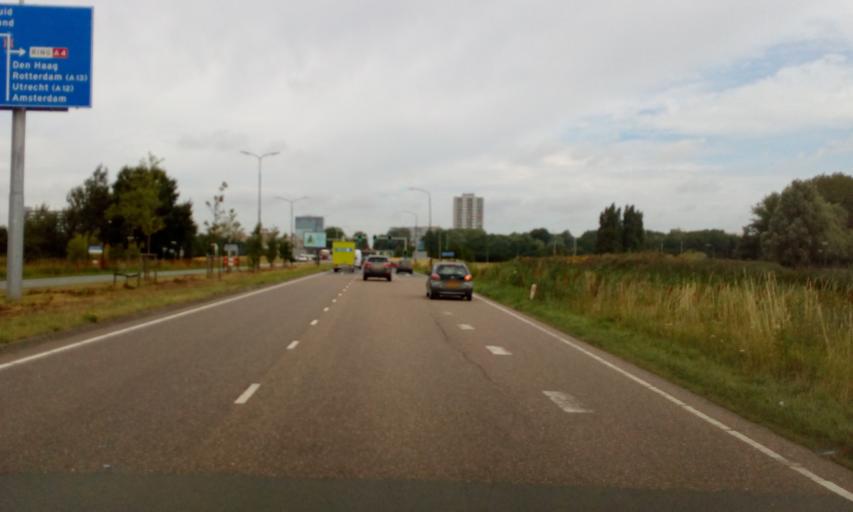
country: NL
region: South Holland
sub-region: Gemeente Rijswijk
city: Rijswijk
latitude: 52.0246
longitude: 4.3257
